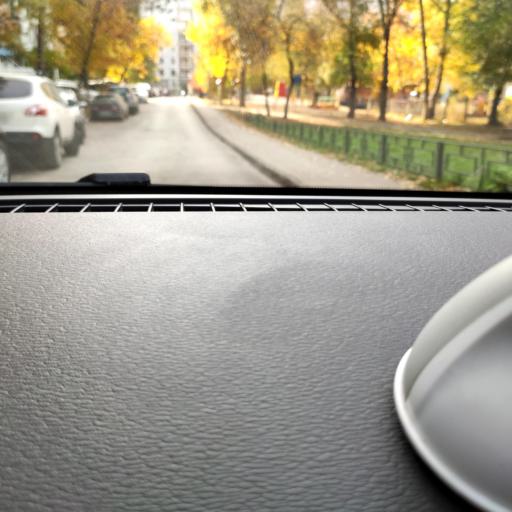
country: RU
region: Samara
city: Samara
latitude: 53.1966
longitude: 50.1422
